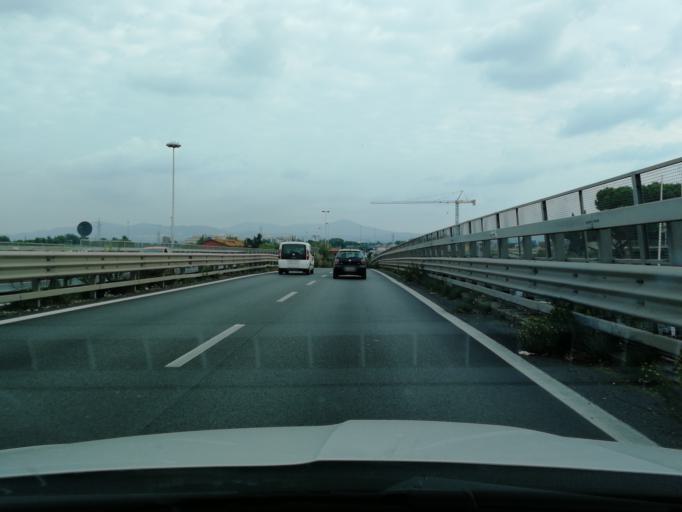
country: IT
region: Latium
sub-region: Citta metropolitana di Roma Capitale
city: Ciampino
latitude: 41.8418
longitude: 12.5852
